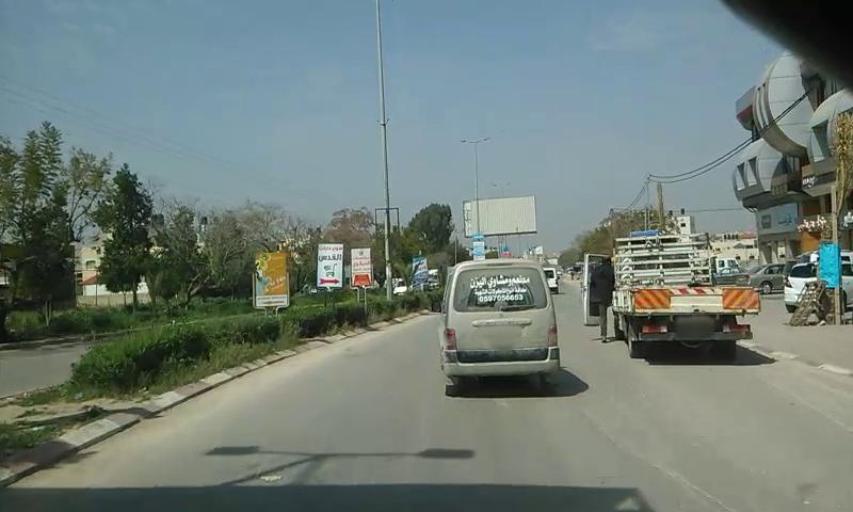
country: PS
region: West Bank
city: Janin
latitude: 32.4707
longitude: 35.3035
